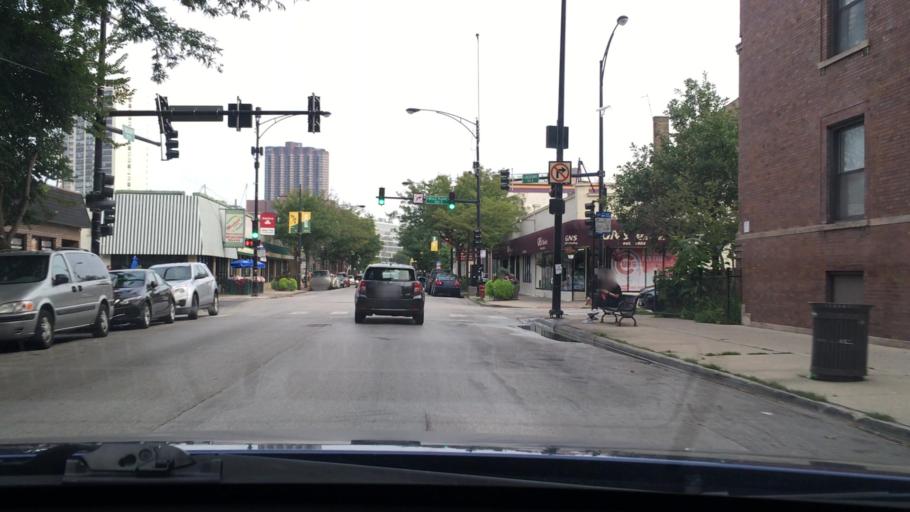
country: US
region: Illinois
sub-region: Cook County
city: Lincolnwood
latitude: 41.9572
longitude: -87.6523
